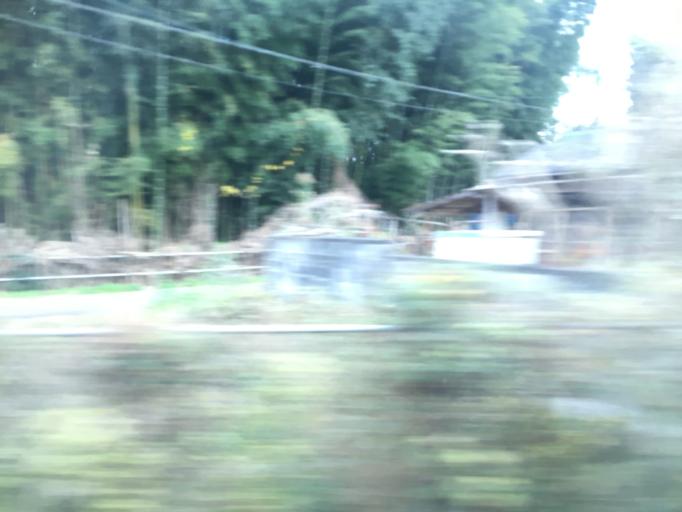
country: JP
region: Ibaraki
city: Kasama
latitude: 36.3711
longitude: 140.2526
